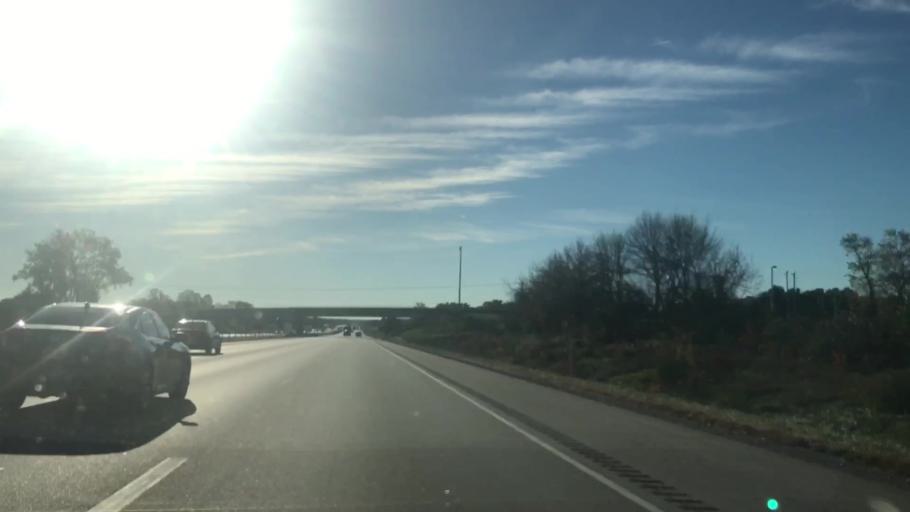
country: US
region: Wisconsin
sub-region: Washington County
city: Richfield
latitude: 43.2377
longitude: -88.1763
